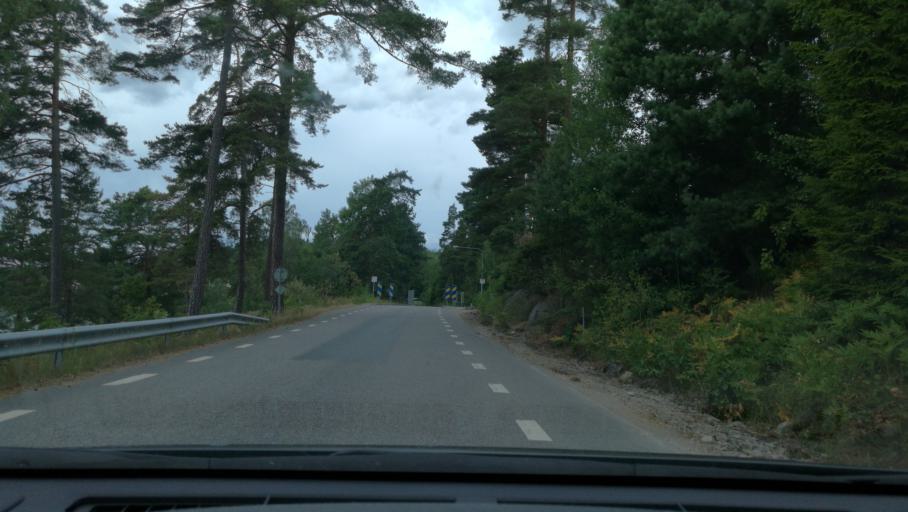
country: SE
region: OEstergoetland
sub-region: Norrkopings Kommun
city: Krokek
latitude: 58.6657
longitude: 16.3557
